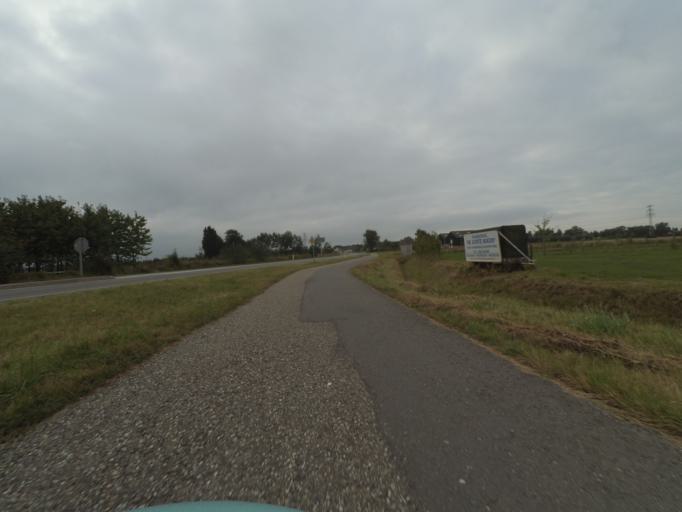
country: NL
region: Utrecht
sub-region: Gemeente Wijk bij Duurstede
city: Wijk bij Duurstede
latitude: 51.9360
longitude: 5.3113
